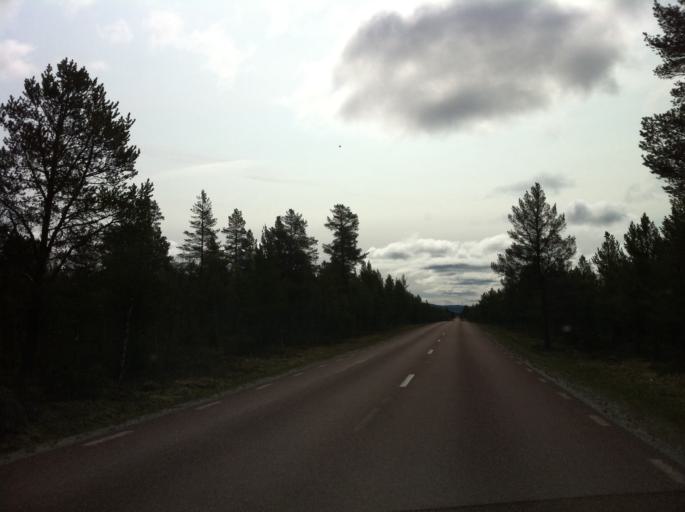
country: NO
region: Hedmark
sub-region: Engerdal
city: Engerdal
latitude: 62.4860
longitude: 12.6525
